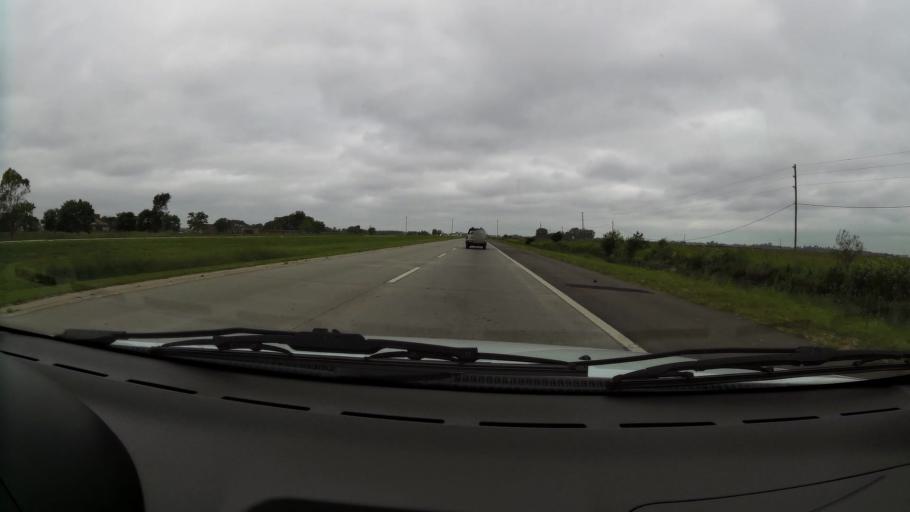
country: AR
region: Buenos Aires
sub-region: Partido de Brandsen
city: Brandsen
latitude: -35.0403
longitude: -58.1796
